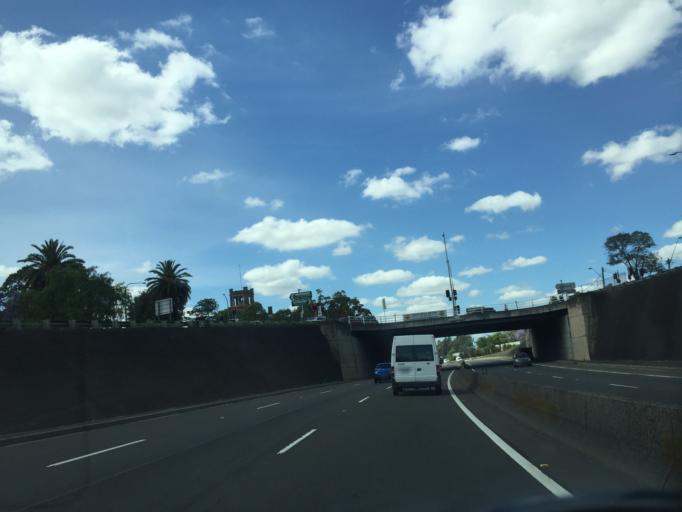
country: AU
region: New South Wales
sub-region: Parramatta
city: Paramatta
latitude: -33.7948
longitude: 151.0134
